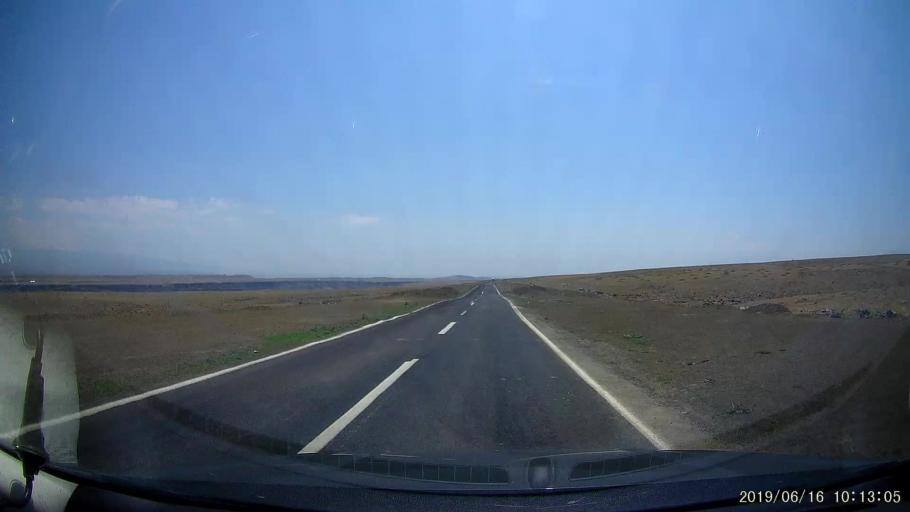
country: TR
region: Igdir
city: Tuzluca
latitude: 40.1938
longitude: 43.6352
